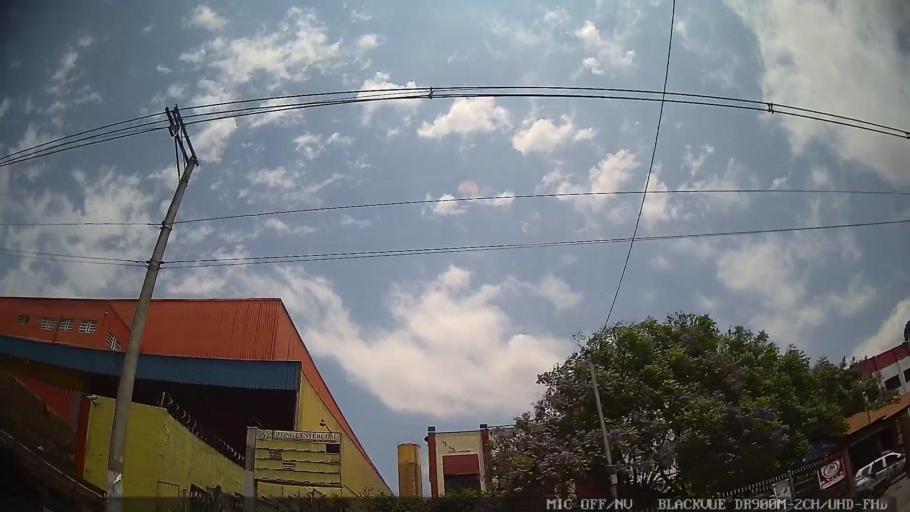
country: BR
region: Sao Paulo
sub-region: Caieiras
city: Caieiras
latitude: -23.4397
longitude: -46.7214
